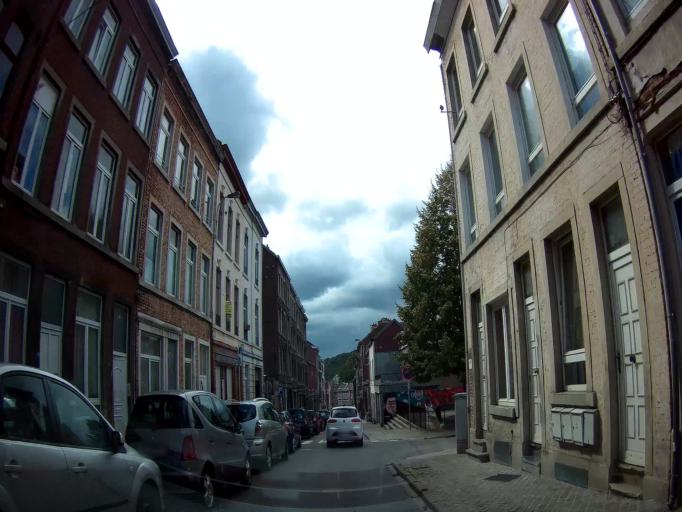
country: BE
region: Wallonia
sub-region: Province de Liege
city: Verviers
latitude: 50.5975
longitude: 5.8565
